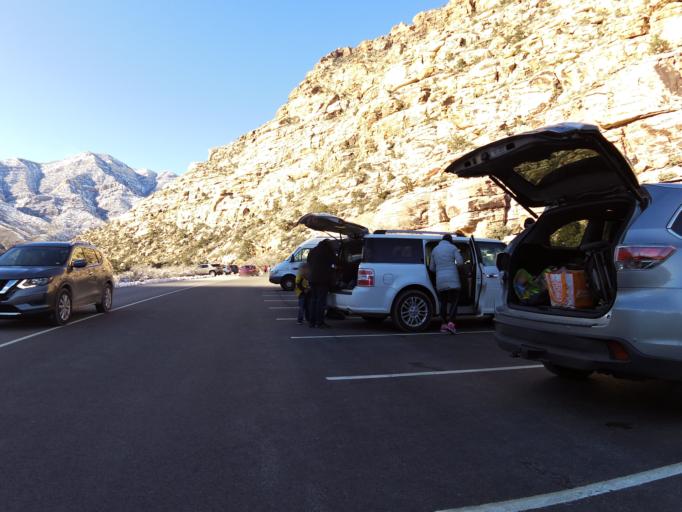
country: US
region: Nevada
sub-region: Clark County
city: Summerlin South
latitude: 36.1603
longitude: -115.4981
